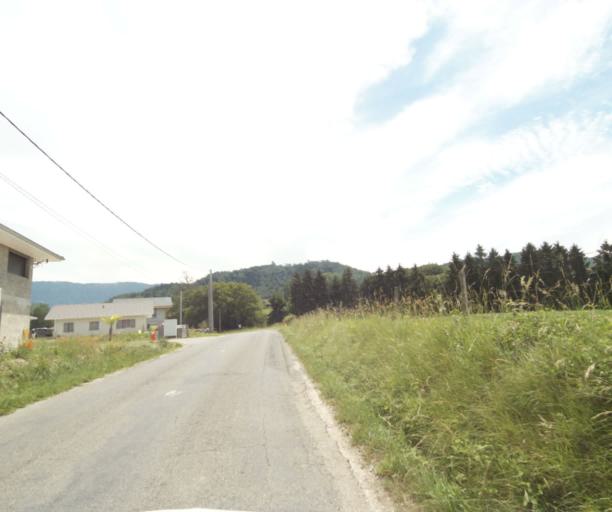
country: FR
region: Rhone-Alpes
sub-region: Departement de la Haute-Savoie
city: Allinges
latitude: 46.3424
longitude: 6.4574
